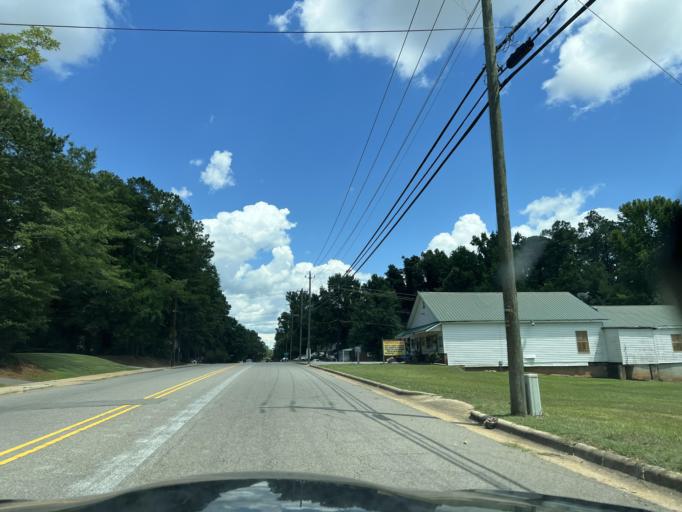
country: US
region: North Carolina
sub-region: Lee County
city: Sanford
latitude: 35.4673
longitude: -79.1673
